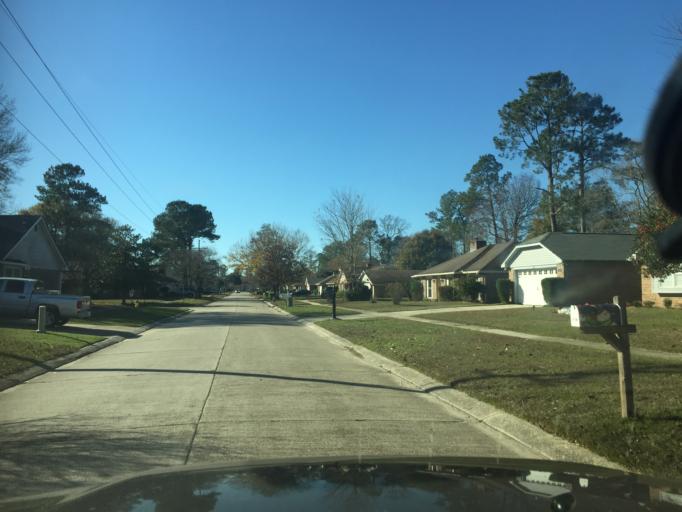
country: US
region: Louisiana
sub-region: Saint Tammany Parish
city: Slidell
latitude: 30.2934
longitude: -89.7506
